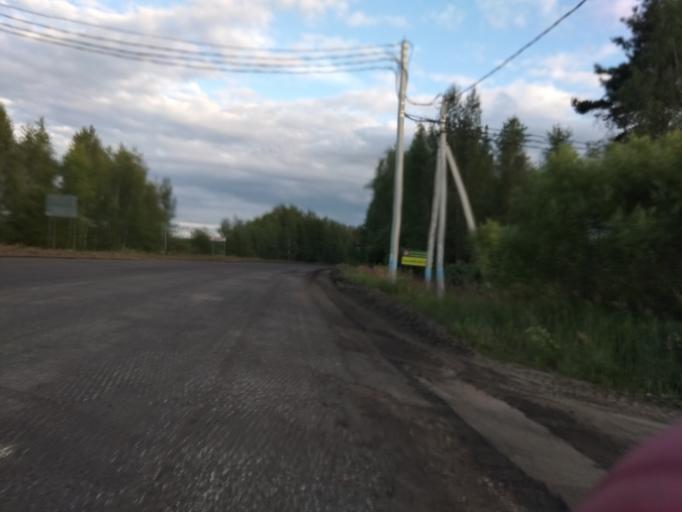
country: RU
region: Moskovskaya
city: Misheronskiy
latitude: 55.6483
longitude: 39.7569
